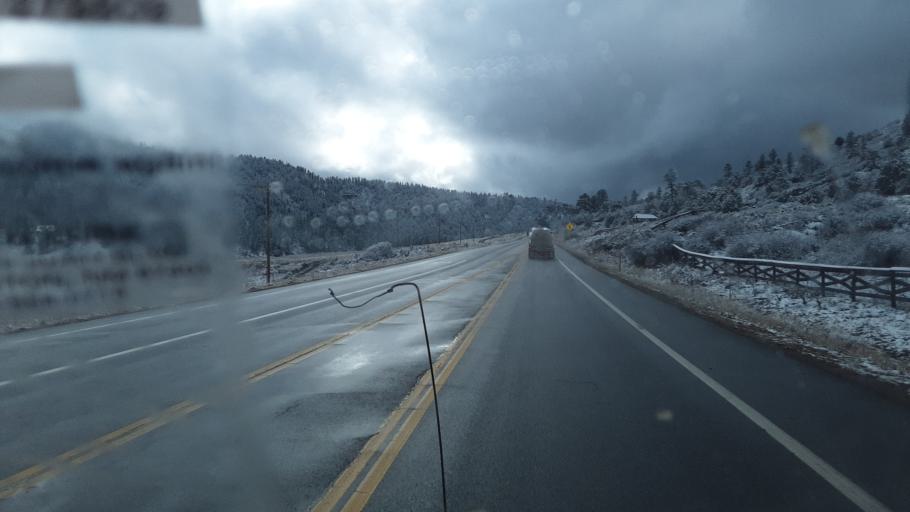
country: US
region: Colorado
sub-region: Archuleta County
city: Pagosa Springs
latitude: 37.2230
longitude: -107.2178
